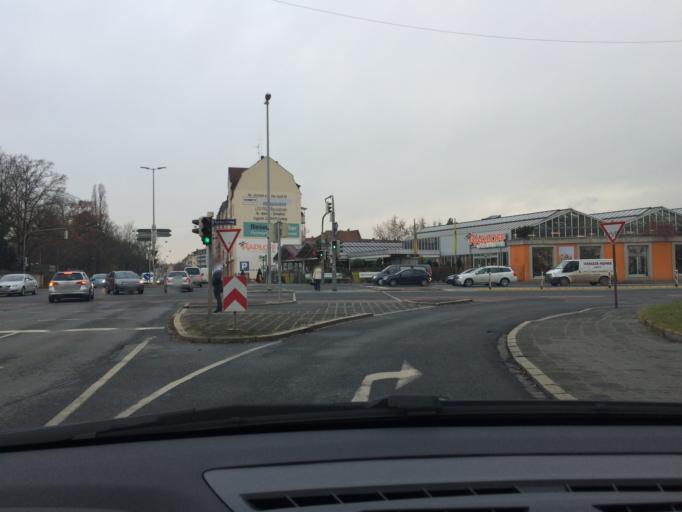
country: DE
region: Bavaria
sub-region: Regierungsbezirk Mittelfranken
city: Wetzendorf
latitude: 49.4632
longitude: 11.0519
